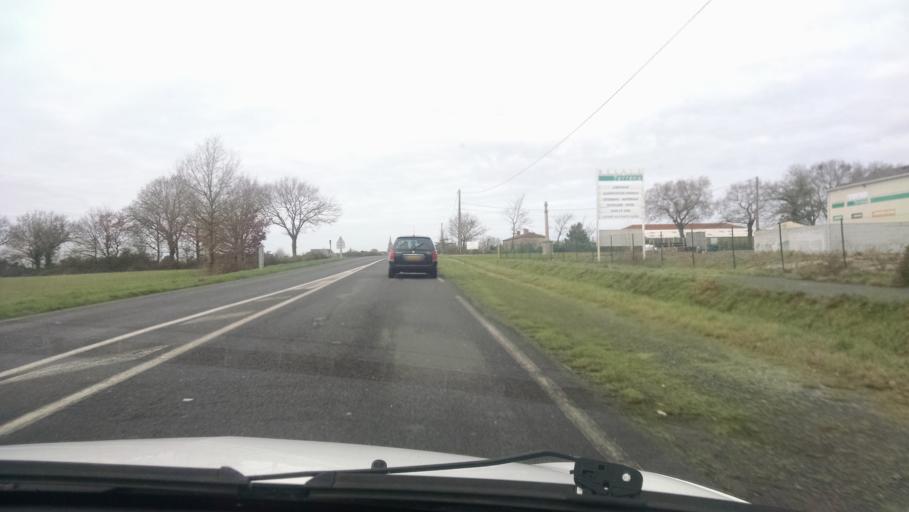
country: FR
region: Pays de la Loire
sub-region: Departement de Maine-et-Loire
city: Torfou
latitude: 47.0342
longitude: -1.1035
